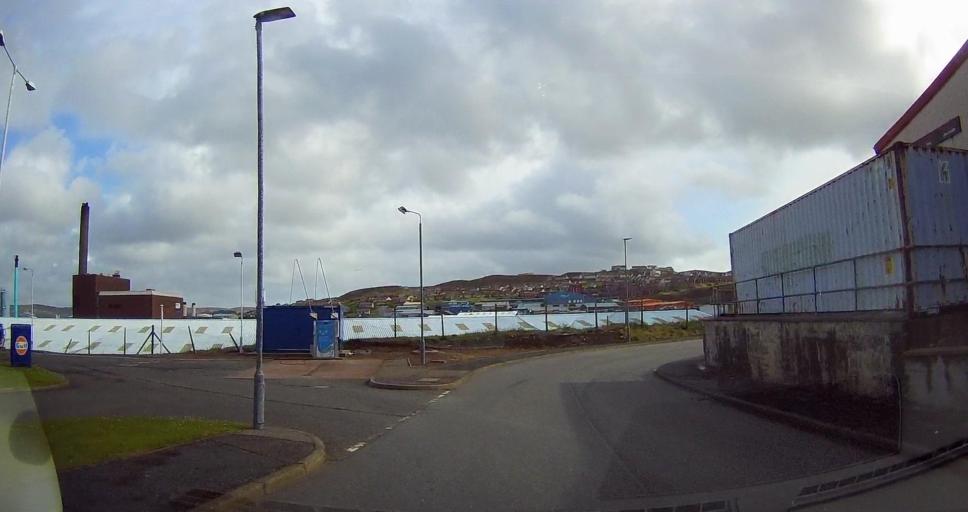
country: GB
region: Scotland
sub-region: Shetland Islands
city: Lerwick
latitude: 60.1692
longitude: -1.1677
